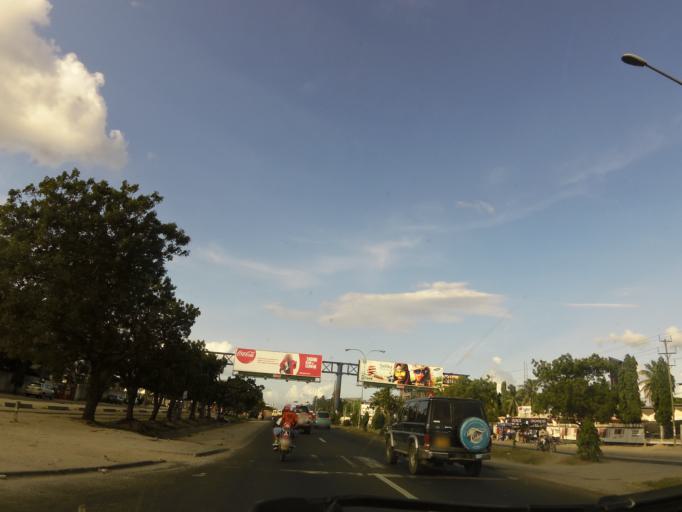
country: TZ
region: Dar es Salaam
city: Dar es Salaam
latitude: -6.8525
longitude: 39.2284
